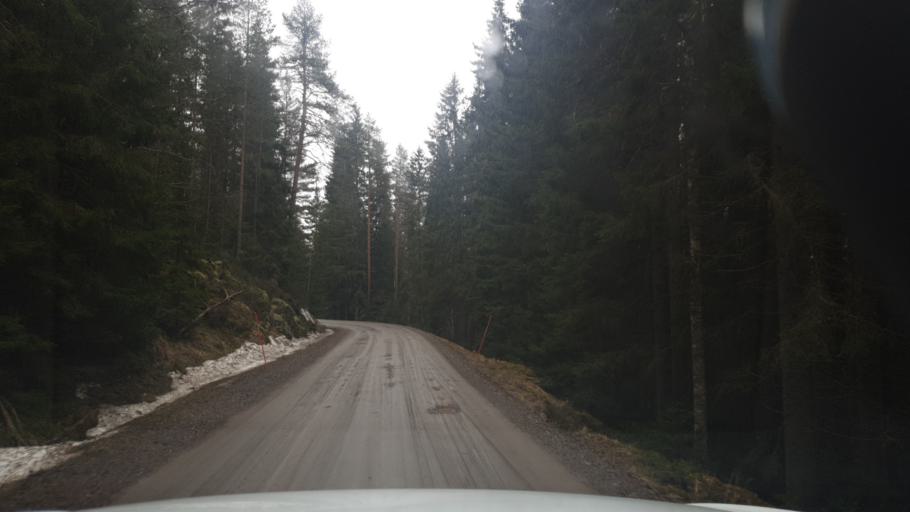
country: NO
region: Ostfold
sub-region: Romskog
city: Romskog
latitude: 59.7123
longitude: 12.0234
